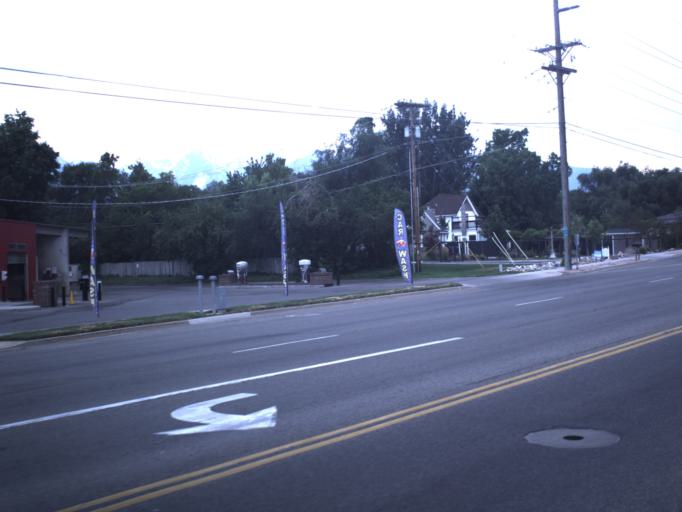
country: US
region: Utah
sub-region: Salt Lake County
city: Murray
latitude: 40.6417
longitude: -111.8661
